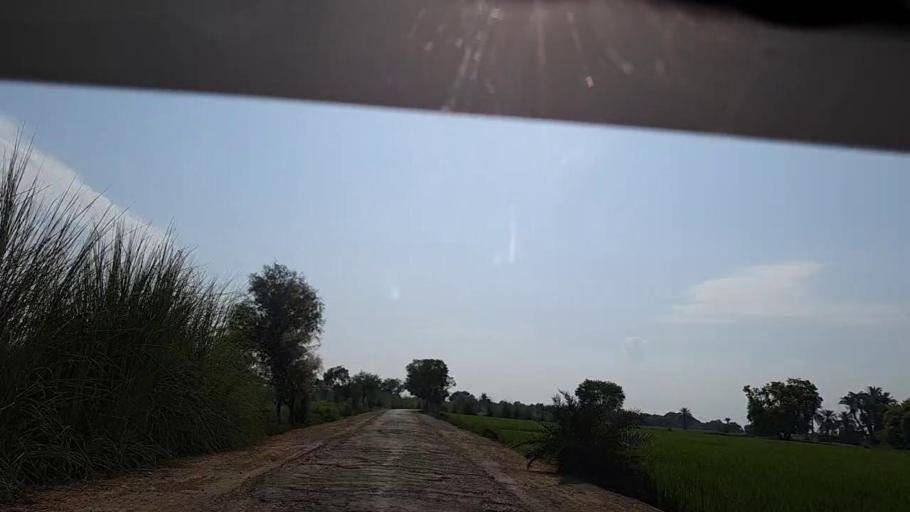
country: PK
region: Sindh
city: Shikarpur
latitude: 28.0877
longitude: 68.6686
